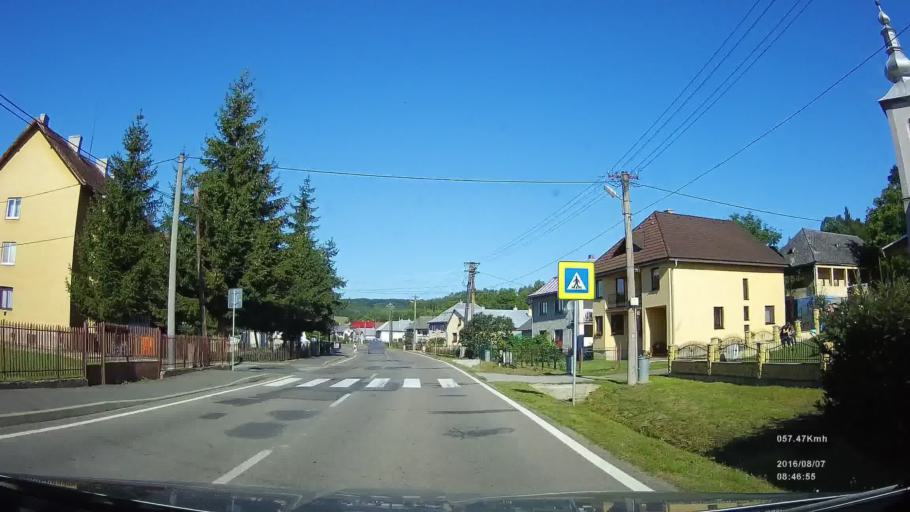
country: SK
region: Presovsky
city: Stropkov
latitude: 49.2659
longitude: 21.7163
